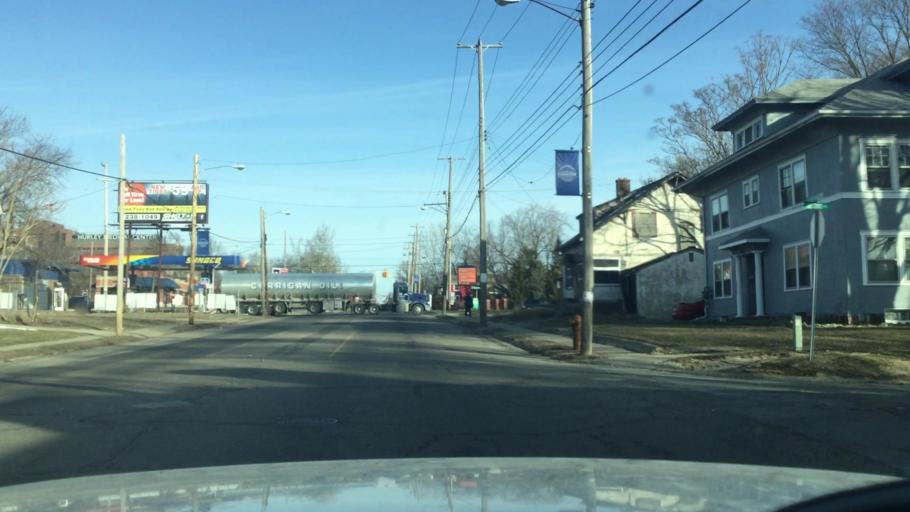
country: US
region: Michigan
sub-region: Genesee County
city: Flint
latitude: 43.0181
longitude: -83.6989
